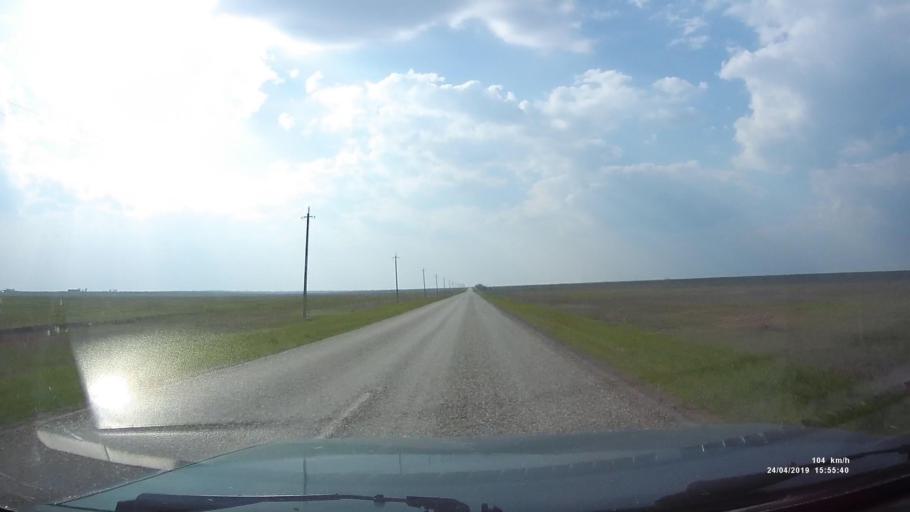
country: RU
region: Kalmykiya
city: Yashalta
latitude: 46.5921
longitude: 42.5446
